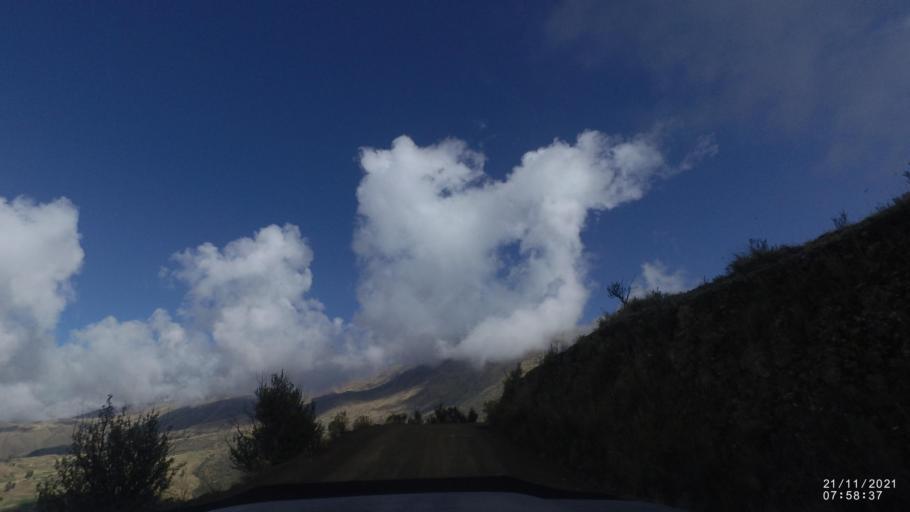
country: BO
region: Cochabamba
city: Cochabamba
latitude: -17.2939
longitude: -66.2202
